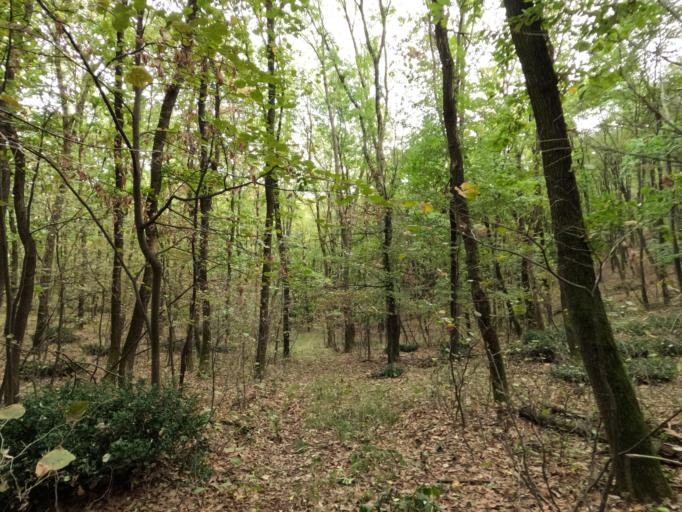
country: HU
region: Tolna
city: Szekszard
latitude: 46.3155
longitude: 18.6593
